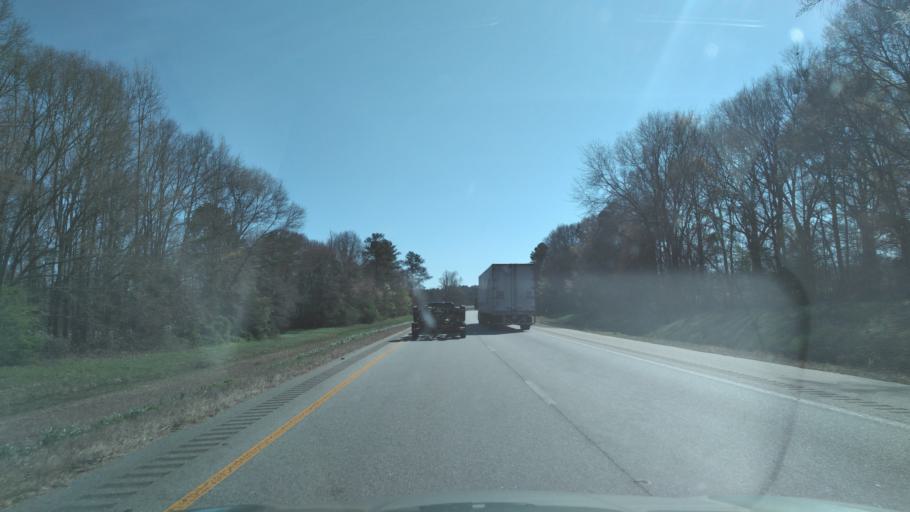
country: US
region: Alabama
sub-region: Lowndes County
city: Fort Deposit
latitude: 31.9681
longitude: -86.5370
